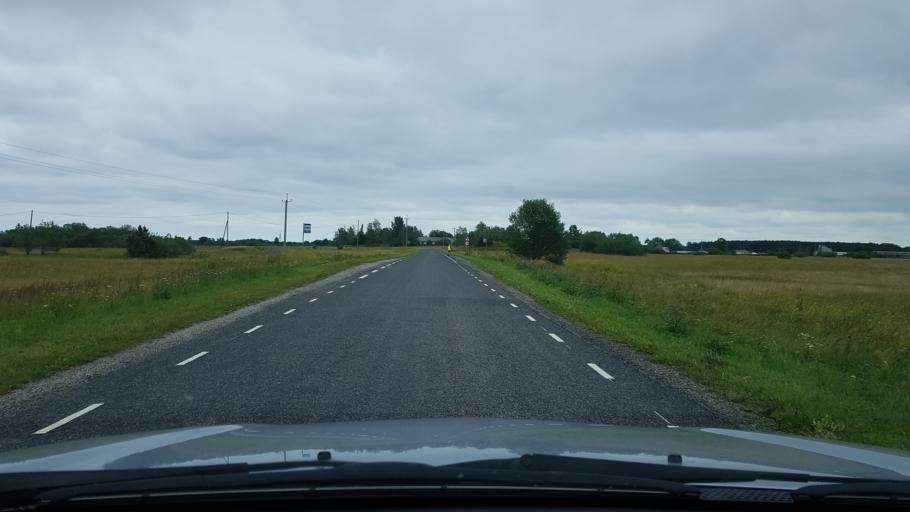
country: EE
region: Ida-Virumaa
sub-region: Narva linn
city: Narva
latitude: 59.3810
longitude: 28.1290
